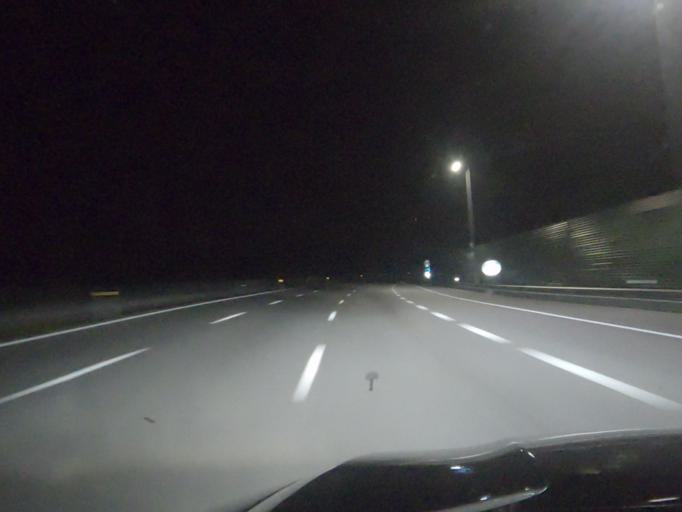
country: PT
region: Coimbra
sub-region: Condeixa-A-Nova
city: Condeixa-a-Nova
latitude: 40.1355
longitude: -8.4959
